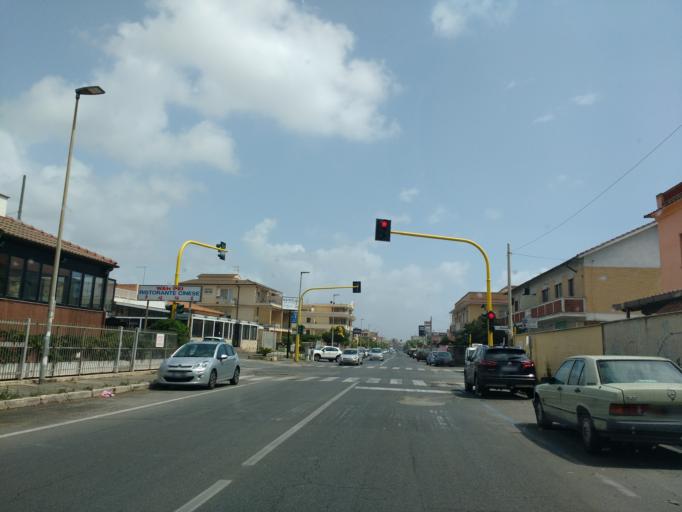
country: IT
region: Latium
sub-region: Citta metropolitana di Roma Capitale
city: Torvaianica
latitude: 41.6478
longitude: 12.4292
